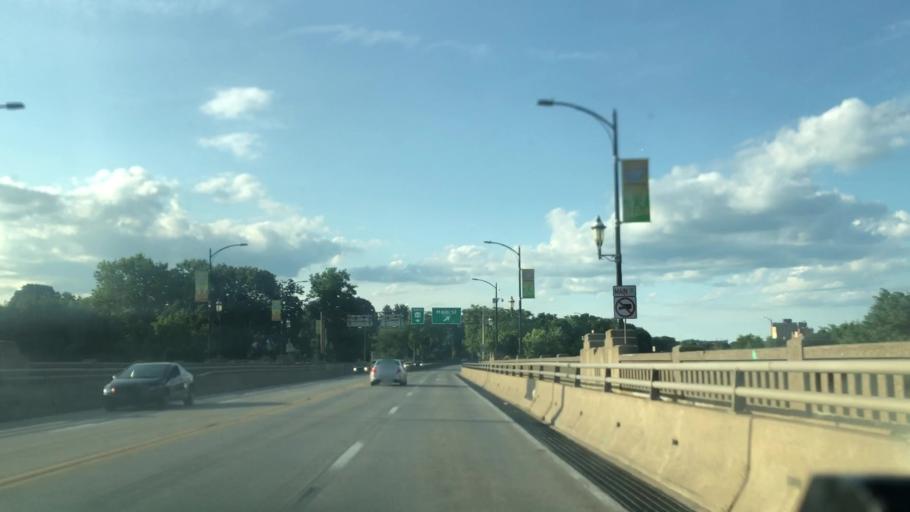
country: US
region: Pennsylvania
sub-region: Northampton County
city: Bethlehem
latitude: 40.6169
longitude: -75.3848
